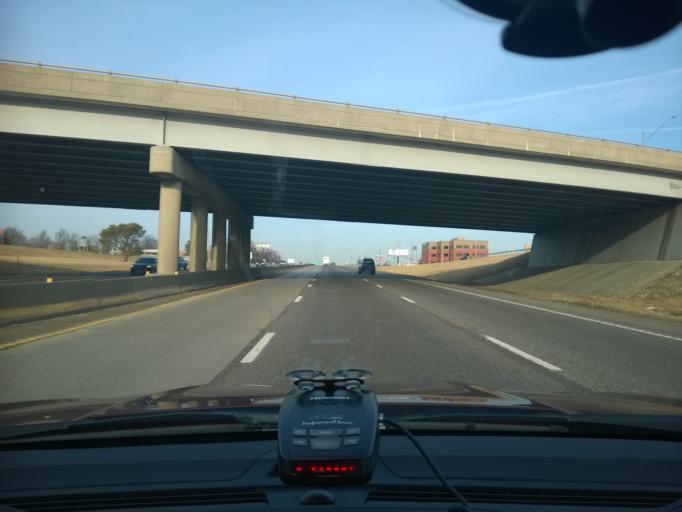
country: US
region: Missouri
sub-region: Saint Charles County
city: Saint Charles
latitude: 38.7868
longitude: -90.5330
